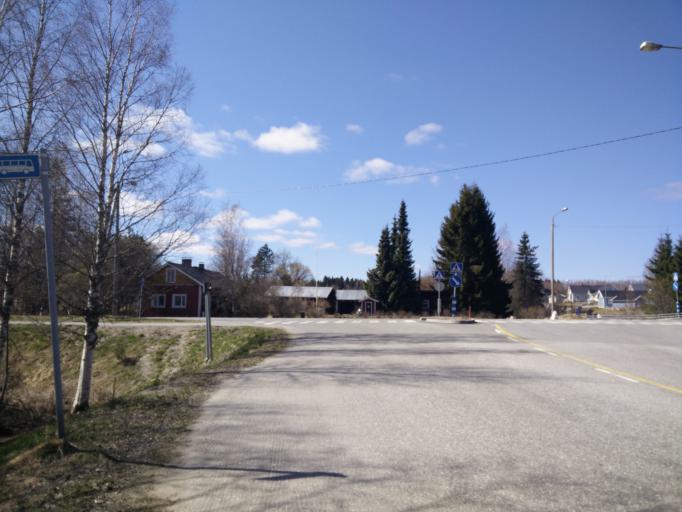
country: FI
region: Pirkanmaa
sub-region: Tampere
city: Orivesi
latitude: 61.6478
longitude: 24.3580
